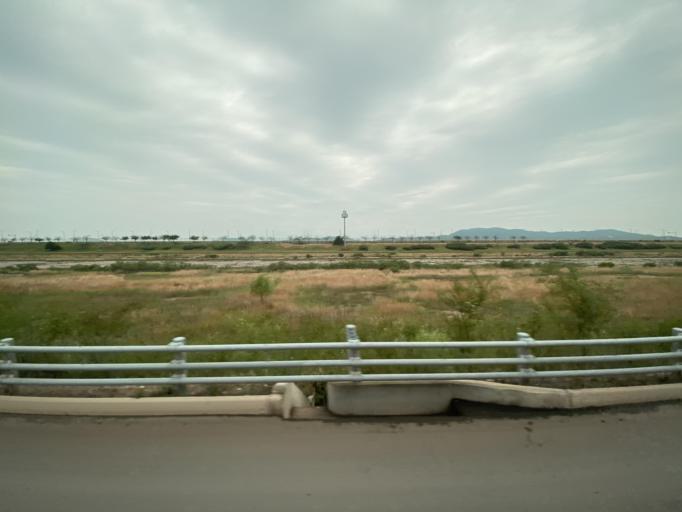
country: KR
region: Incheon
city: Seonwon
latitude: 37.4957
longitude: 126.4286
